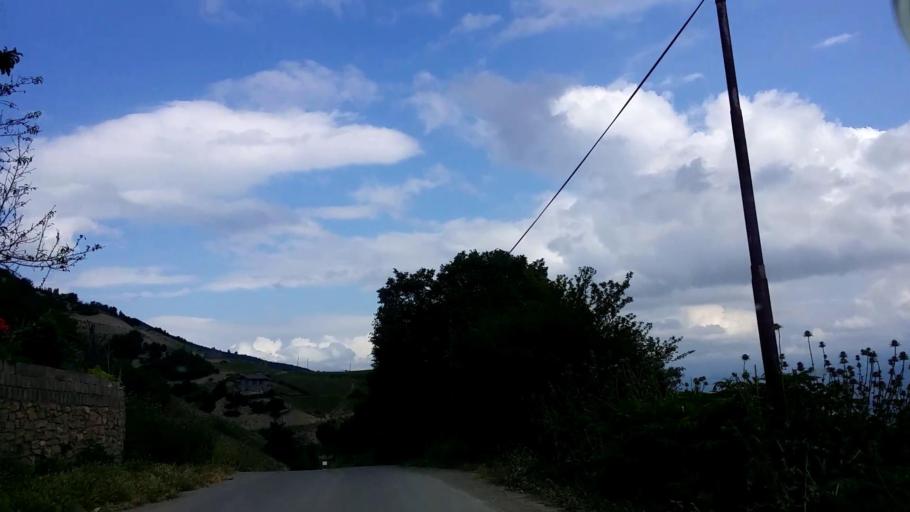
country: IR
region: Mazandaran
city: Chalus
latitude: 36.5541
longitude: 51.2771
